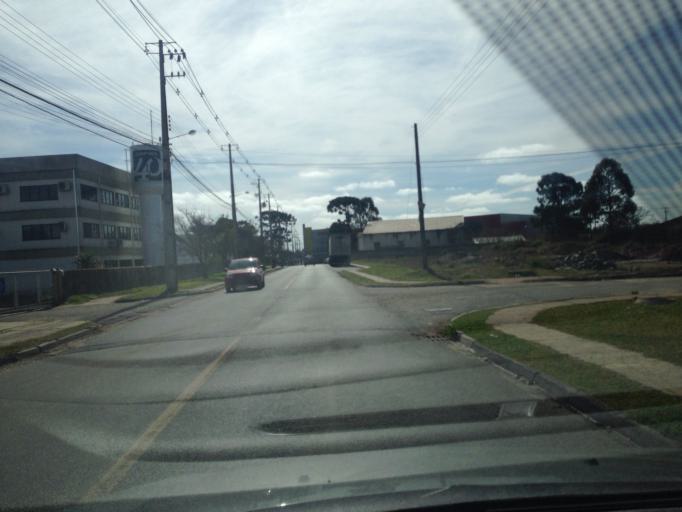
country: BR
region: Parana
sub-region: Sao Jose Dos Pinhais
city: Sao Jose dos Pinhais
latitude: -25.5586
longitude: -49.1709
